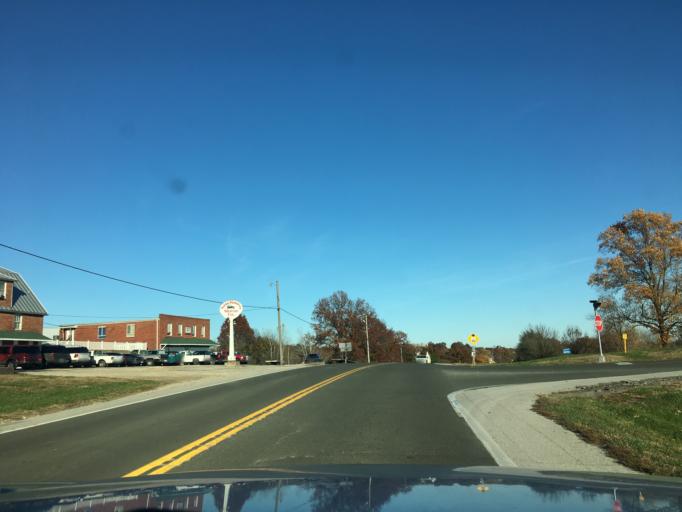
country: US
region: Missouri
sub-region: Franklin County
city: New Haven
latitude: 38.6000
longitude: -91.2414
